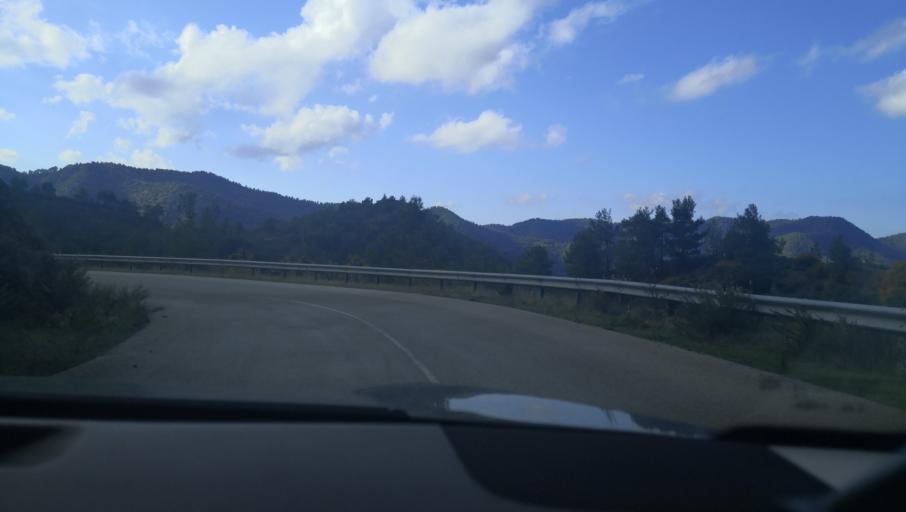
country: CY
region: Lefkosia
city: Lefka
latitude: 35.0532
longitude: 32.7481
